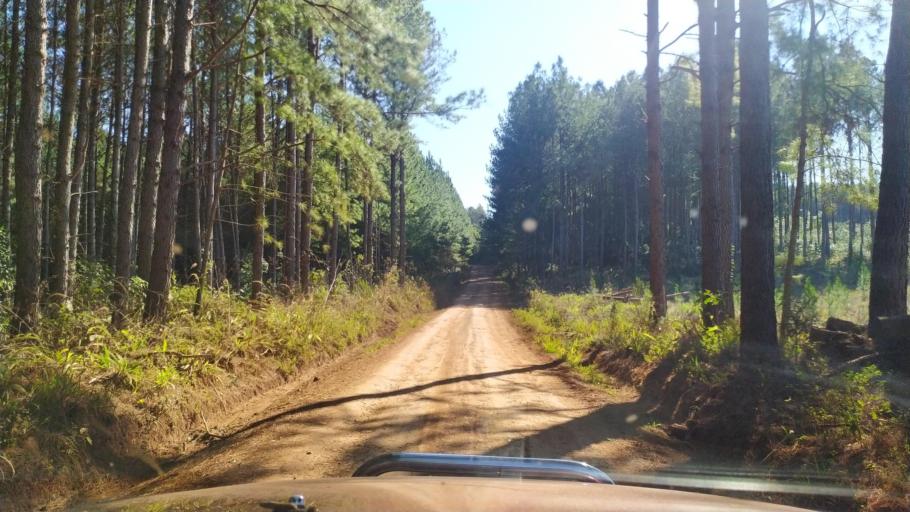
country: AR
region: Misiones
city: El Alcazar
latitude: -26.7306
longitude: -54.6771
